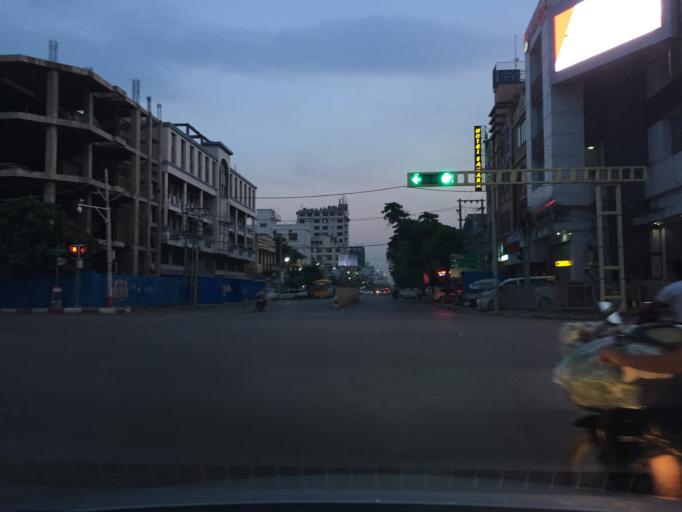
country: MM
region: Mandalay
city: Mandalay
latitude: 21.9833
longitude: 96.0844
